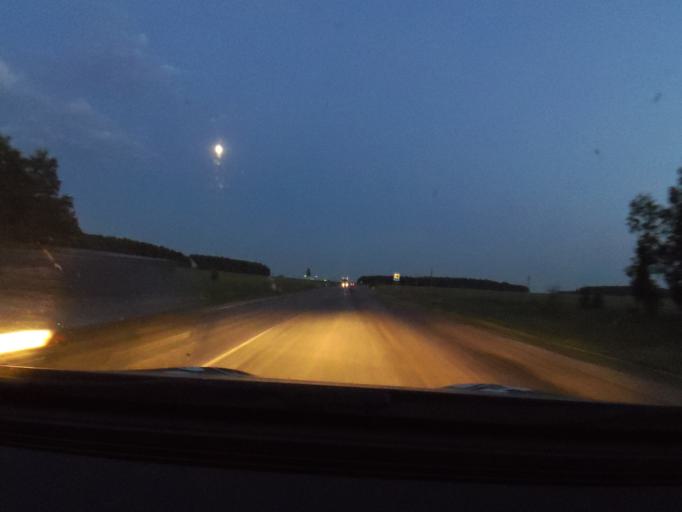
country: RU
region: Bashkortostan
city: Duvan
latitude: 55.9573
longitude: 58.1992
